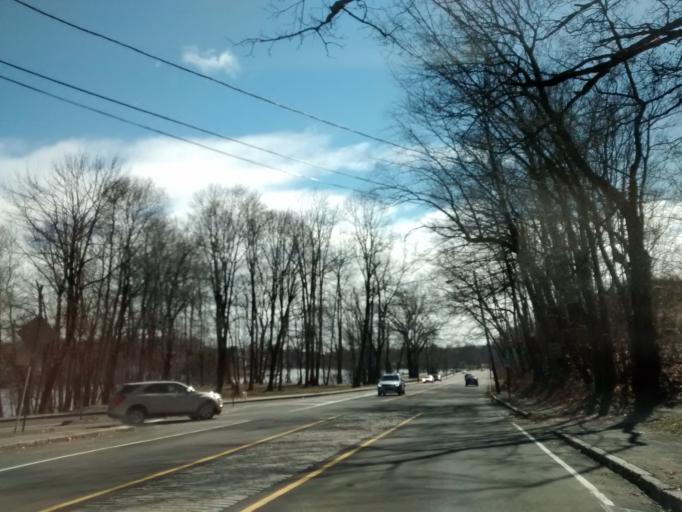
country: US
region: Massachusetts
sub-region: Worcester County
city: Worcester
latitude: 42.2959
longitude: -71.8185
